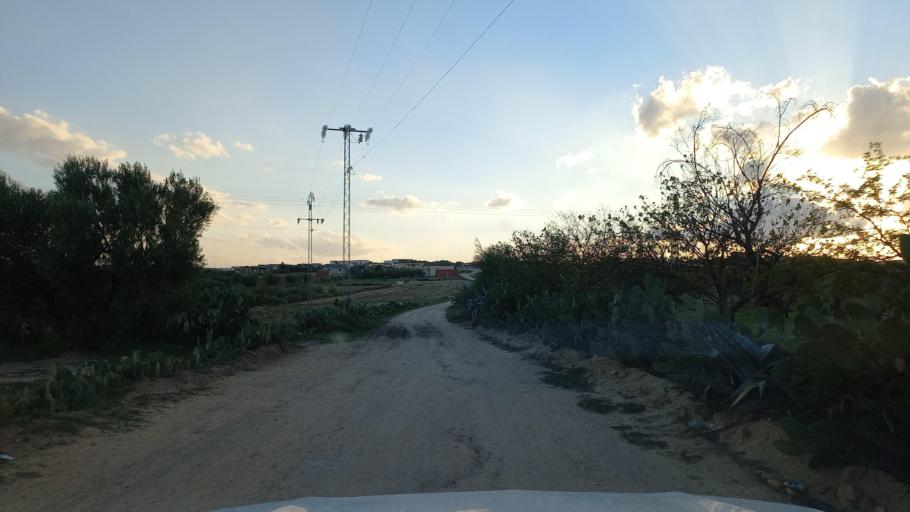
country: TN
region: Al Qasrayn
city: Sbiba
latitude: 35.3737
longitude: 9.0691
